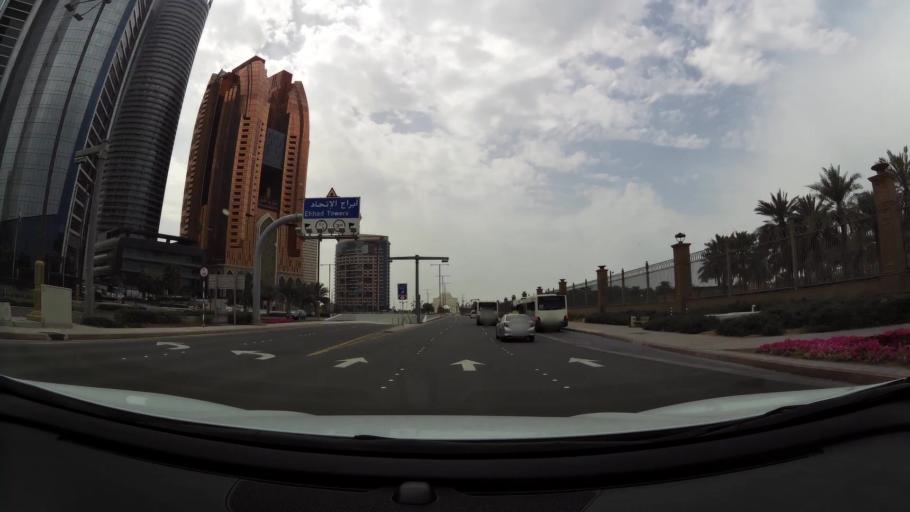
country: AE
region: Abu Dhabi
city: Abu Dhabi
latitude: 24.4604
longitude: 54.3208
